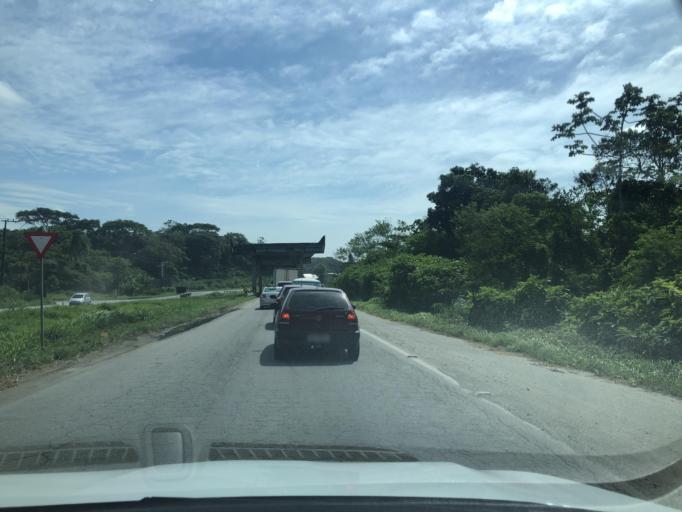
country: BR
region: Santa Catarina
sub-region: Sao Francisco Do Sul
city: Sao Francisco do Sul
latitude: -26.2518
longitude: -48.6111
